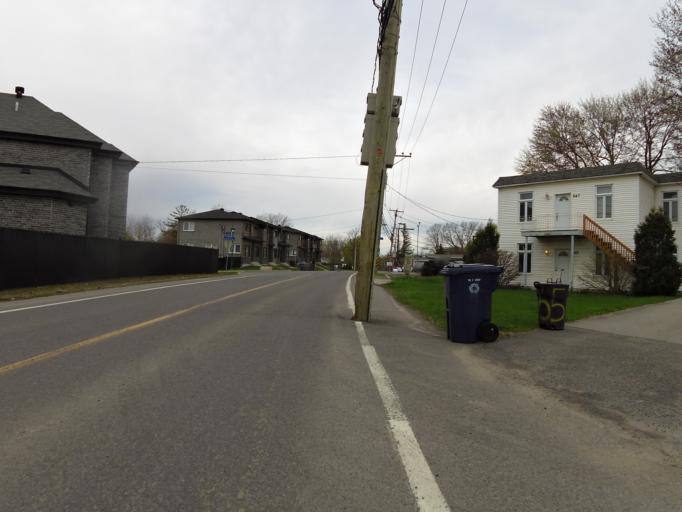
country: CA
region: Quebec
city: Dollard-Des Ormeaux
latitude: 45.5193
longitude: -73.8060
